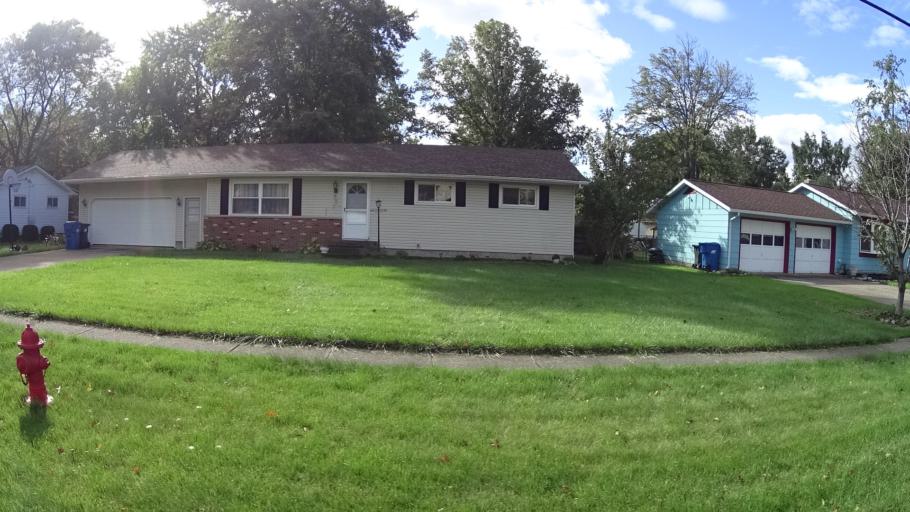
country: US
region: Ohio
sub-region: Lorain County
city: Grafton
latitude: 41.2823
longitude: -82.0615
